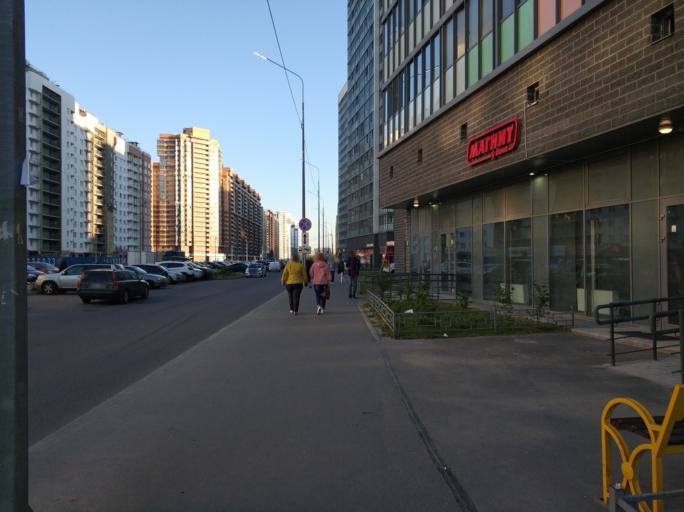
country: RU
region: Leningrad
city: Murino
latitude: 60.0601
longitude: 30.4305
